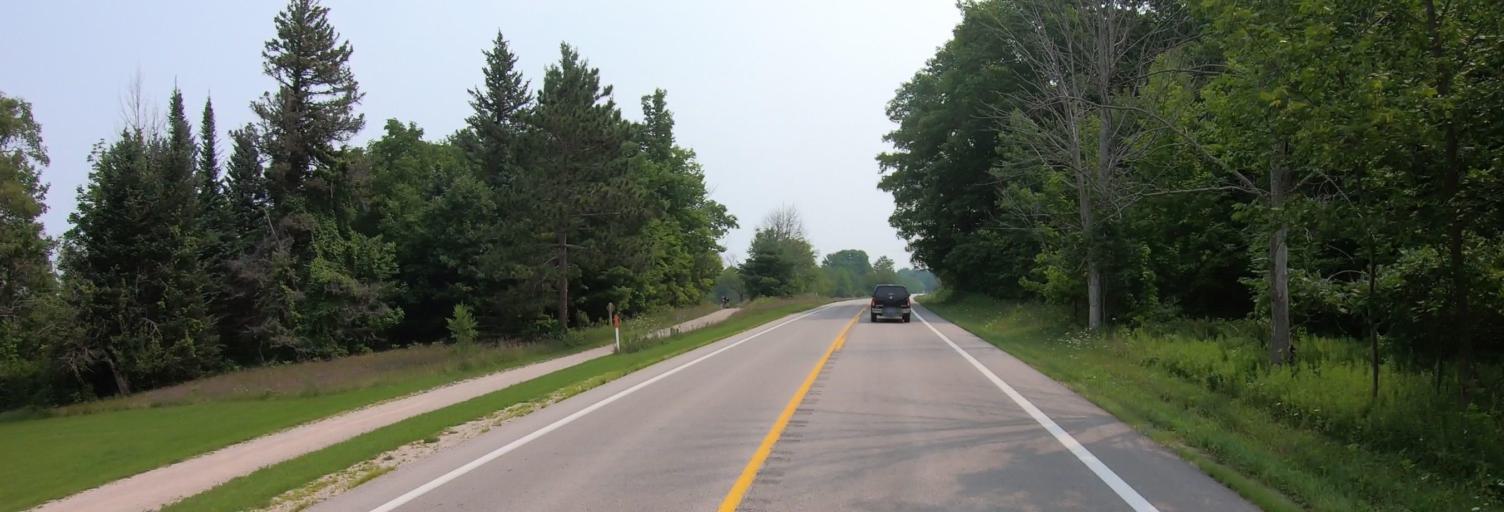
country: US
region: Michigan
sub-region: Leelanau County
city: Leland
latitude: 44.9333
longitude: -85.9040
